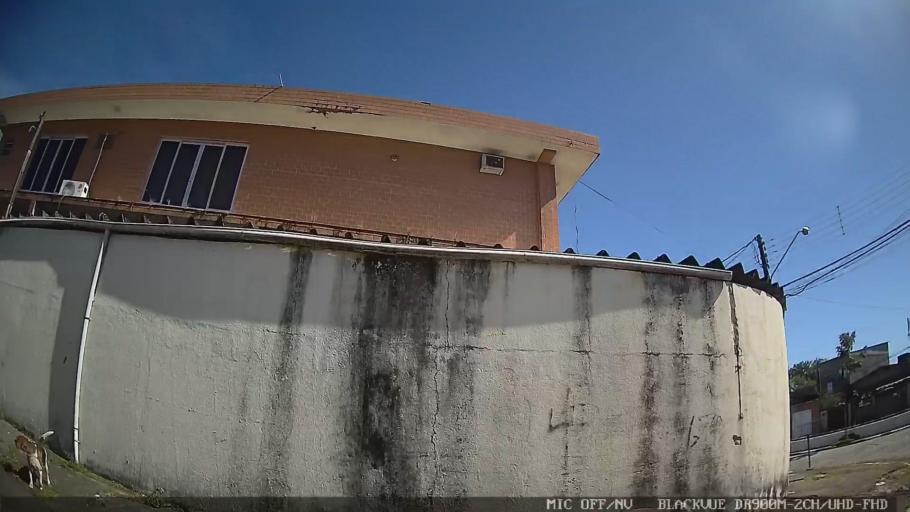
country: BR
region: Sao Paulo
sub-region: Guaruja
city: Guaruja
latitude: -23.9657
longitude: -46.2770
